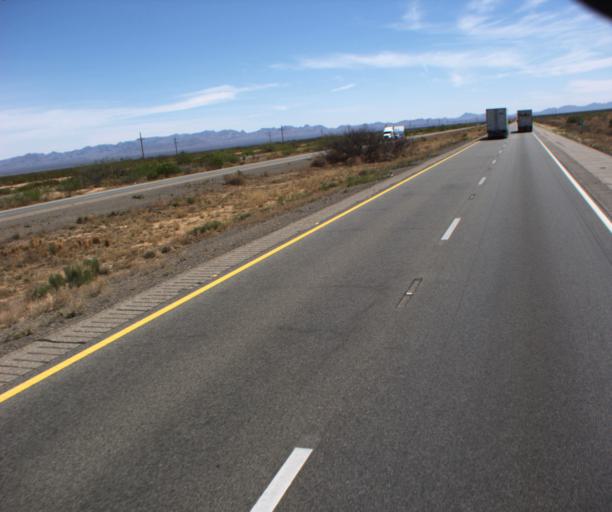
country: US
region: Arizona
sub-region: Cochise County
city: Willcox
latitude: 32.2996
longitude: -109.3648
